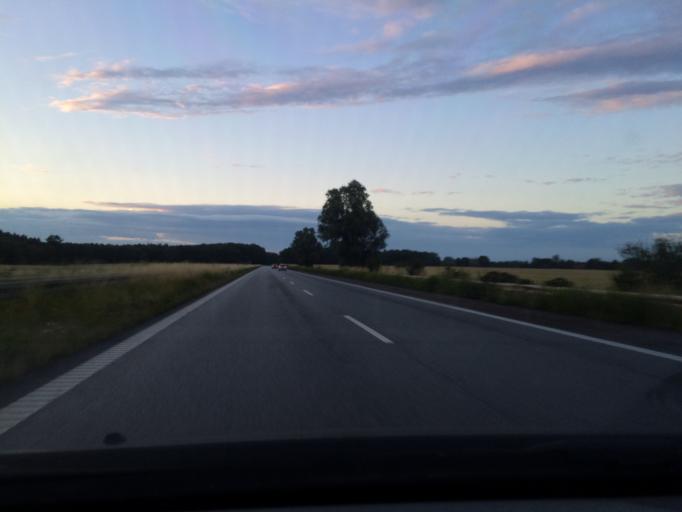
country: DK
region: Zealand
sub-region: Koge Kommune
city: Bjaeverskov
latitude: 55.3588
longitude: 12.0750
